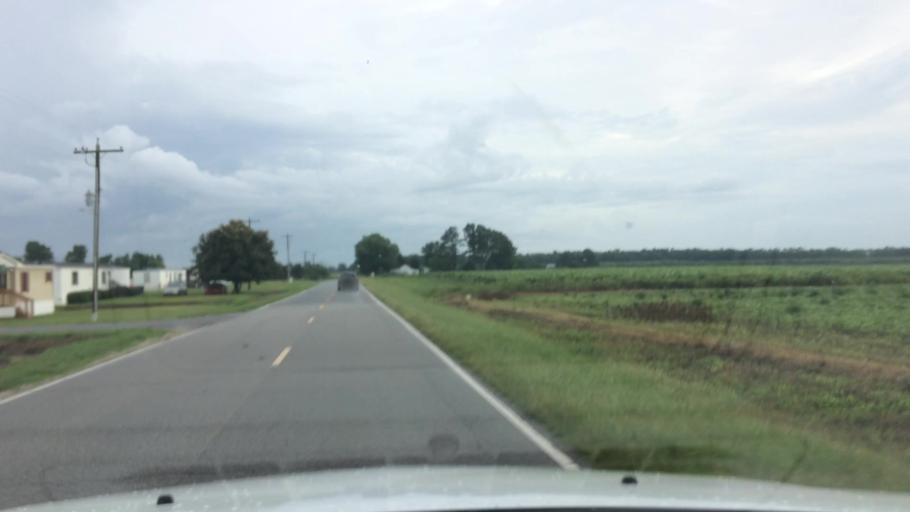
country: US
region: North Carolina
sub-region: Pitt County
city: Farmville
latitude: 35.5596
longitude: -77.5463
